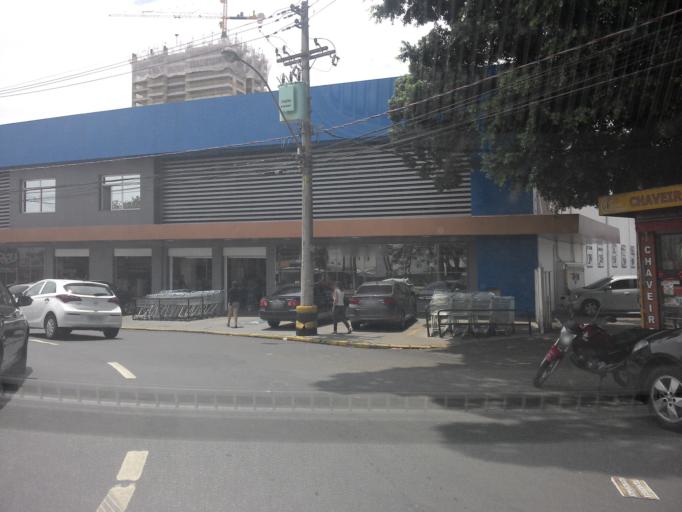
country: BR
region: Sao Paulo
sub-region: Campinas
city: Campinas
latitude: -22.8812
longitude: -47.0503
